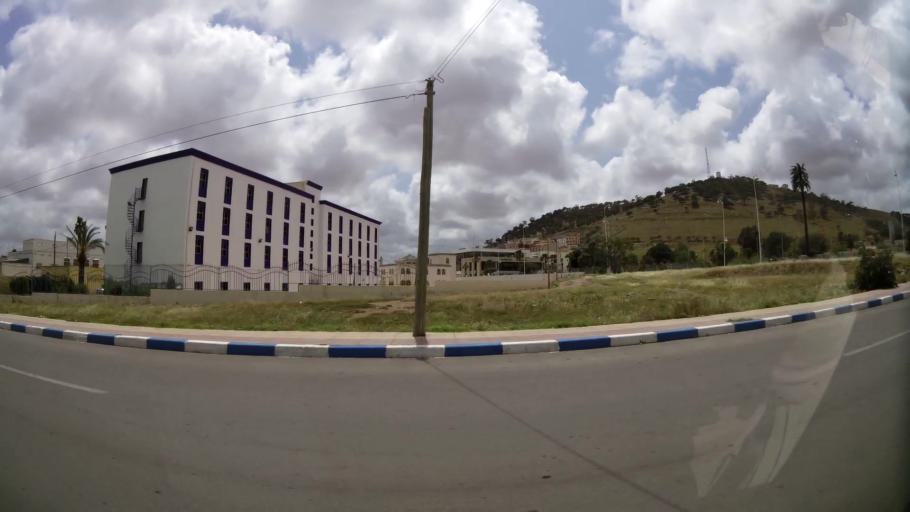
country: MA
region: Oriental
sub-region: Nador
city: Nador
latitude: 35.1854
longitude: -2.9265
